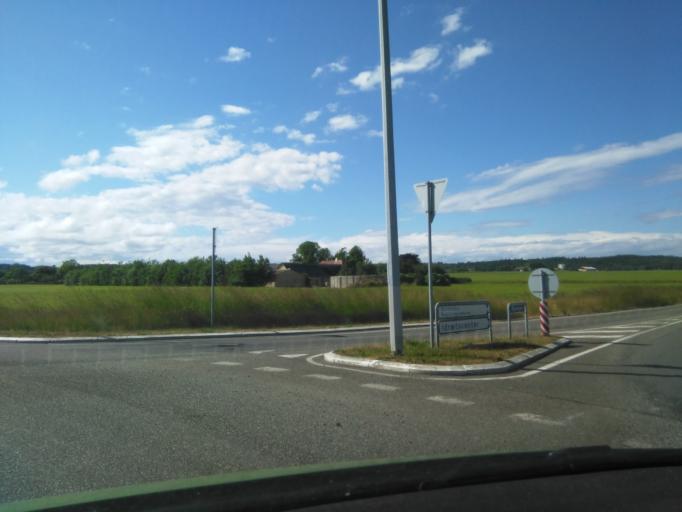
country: DK
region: Capital Region
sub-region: Bornholm Kommune
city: Nexo
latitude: 55.0621
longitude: 15.1137
